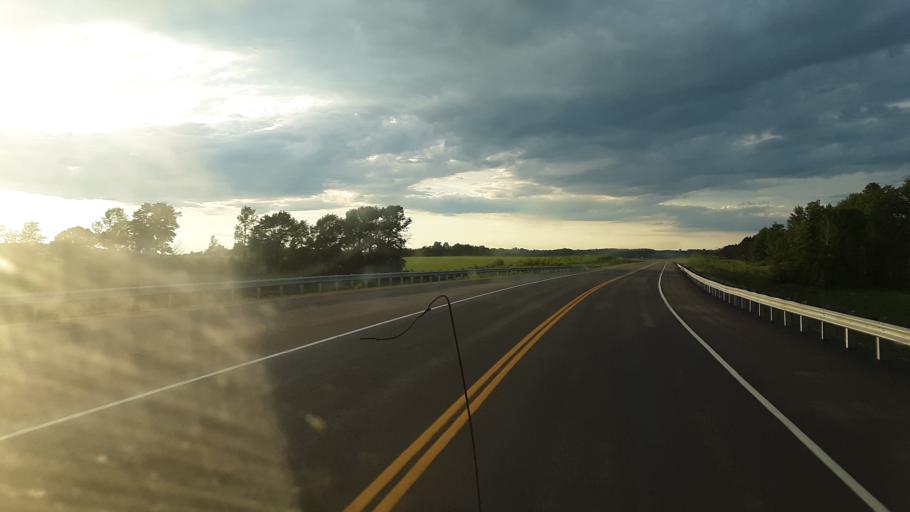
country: US
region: Maine
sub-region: Aroostook County
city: Presque Isle
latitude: 46.6792
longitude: -67.9747
